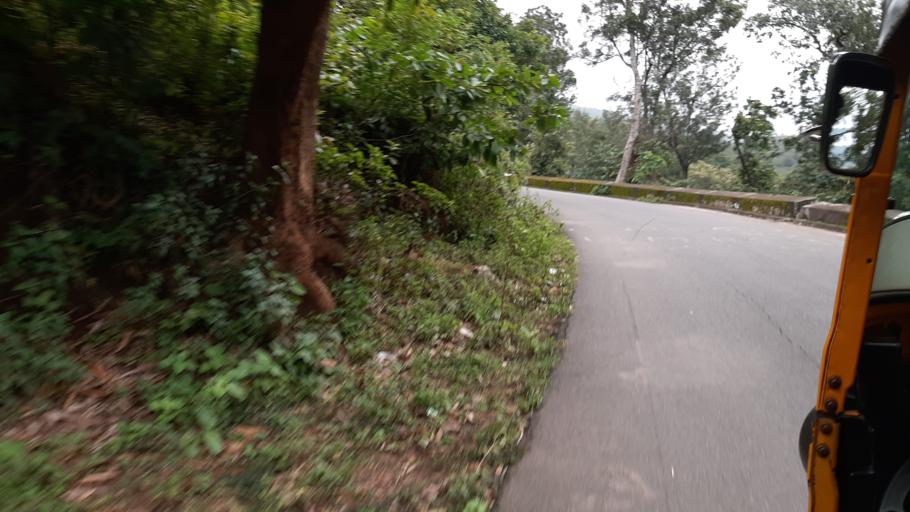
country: IN
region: Andhra Pradesh
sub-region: Vizianagaram District
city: Salur
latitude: 18.2435
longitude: 82.9994
